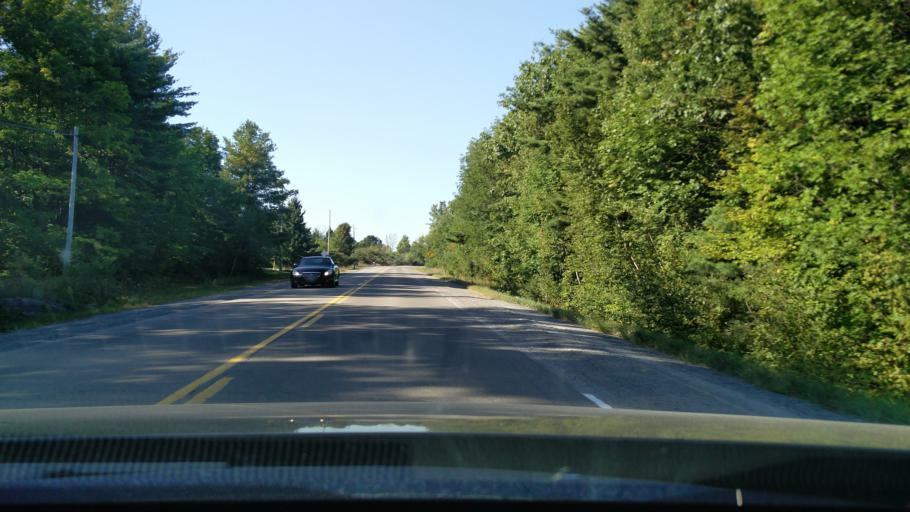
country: CA
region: Ontario
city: Perth
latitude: 44.6914
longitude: -76.3996
